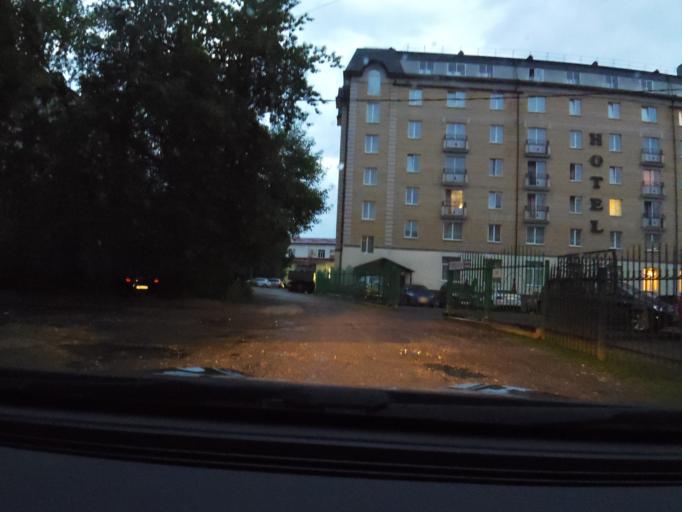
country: RU
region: Vladimir
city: Aleksandrov
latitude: 56.4010
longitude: 38.7262
